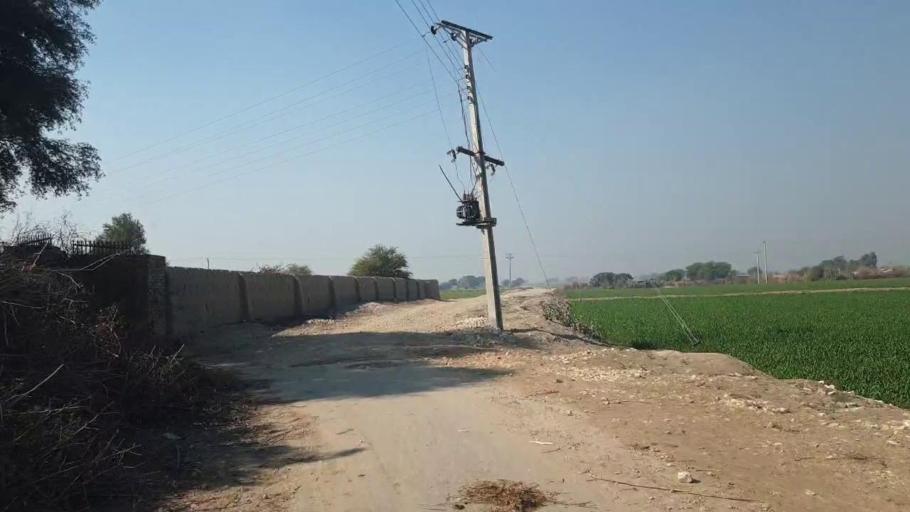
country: PK
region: Sindh
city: Shahpur Chakar
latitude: 26.1095
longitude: 68.6035
